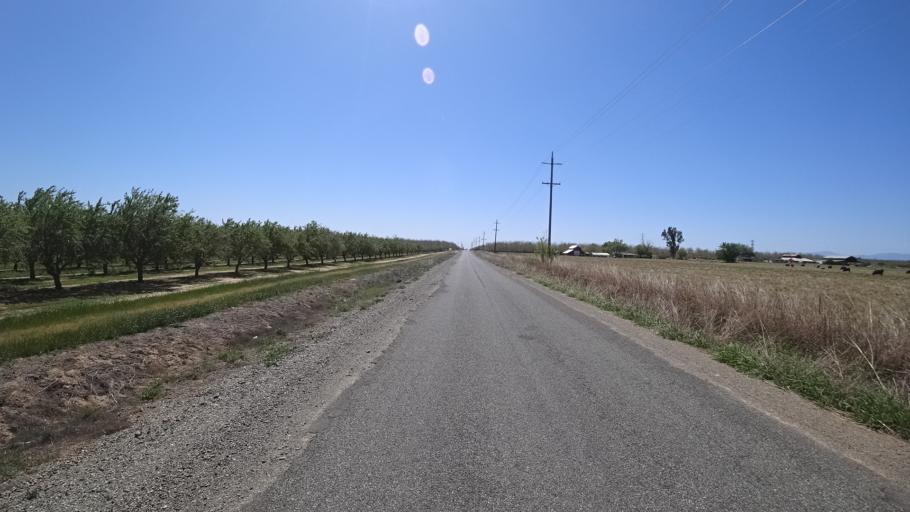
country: US
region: California
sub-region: Glenn County
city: Orland
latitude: 39.7894
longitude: -122.1410
